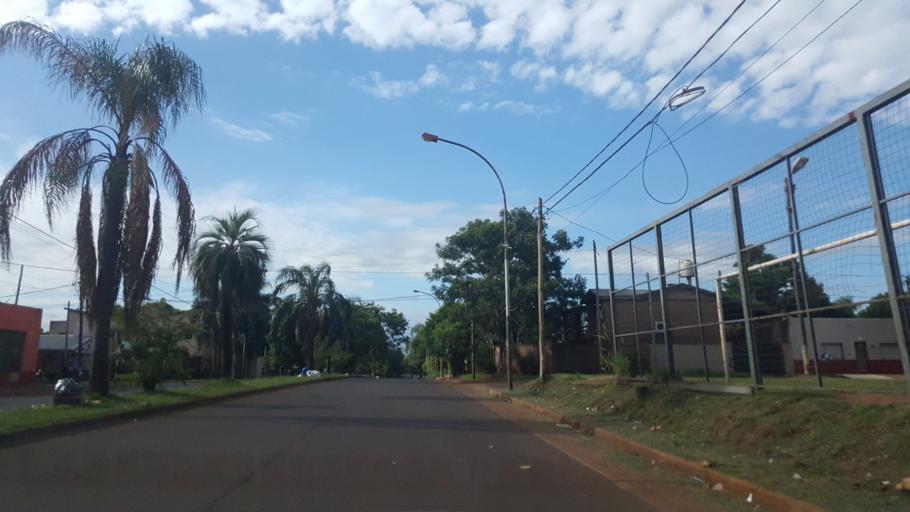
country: AR
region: Misiones
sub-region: Departamento de Capital
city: Posadas
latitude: -27.3667
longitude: -55.9316
